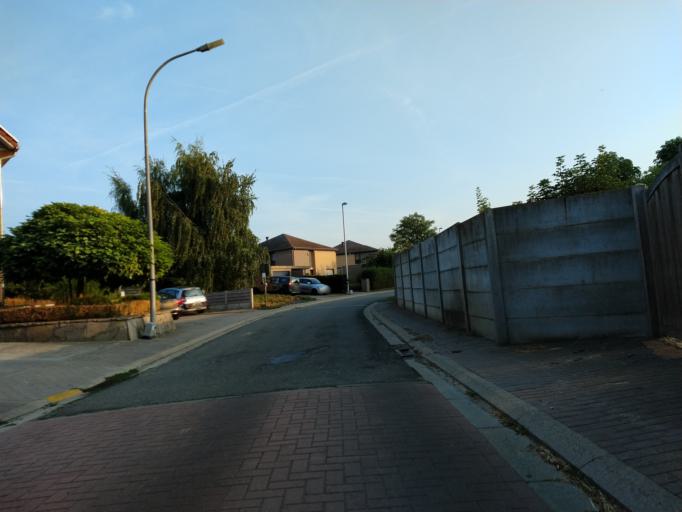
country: BE
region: Flanders
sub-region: Provincie Vlaams-Brabant
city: Hoegaarden
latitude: 50.7726
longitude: 4.8925
